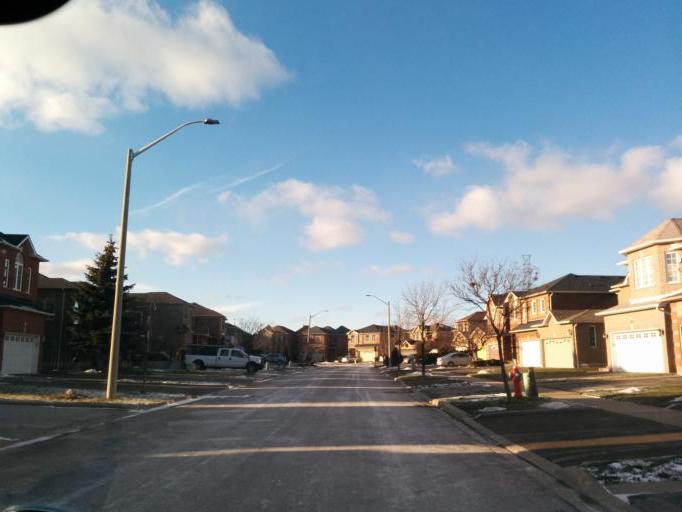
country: CA
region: Ontario
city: Mississauga
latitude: 43.6236
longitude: -79.6462
